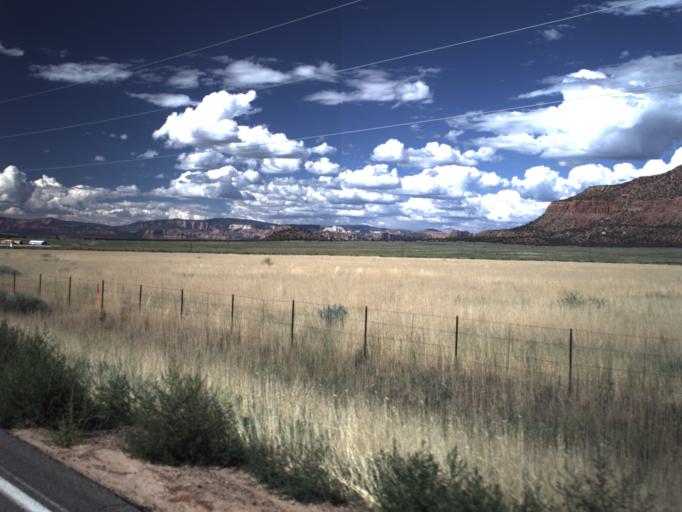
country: US
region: Arizona
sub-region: Mohave County
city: Colorado City
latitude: 37.0909
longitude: -113.1147
